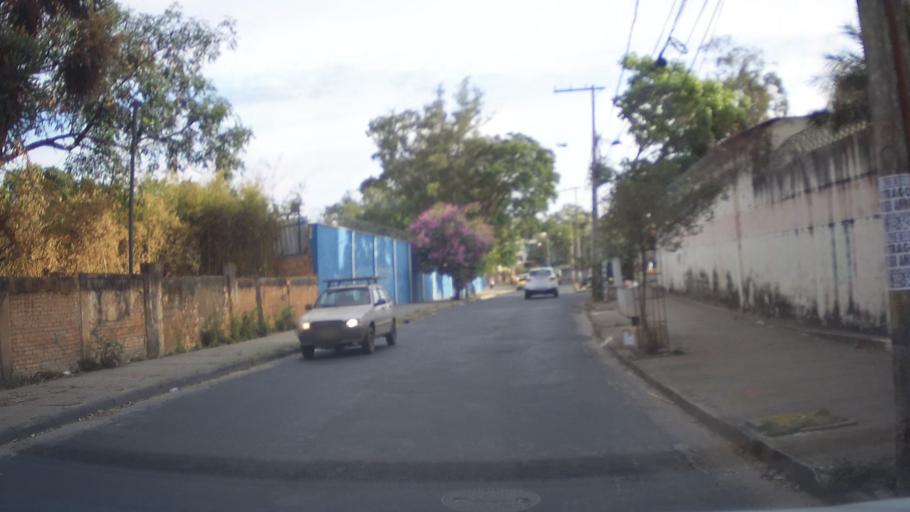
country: BR
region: Minas Gerais
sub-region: Belo Horizonte
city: Belo Horizonte
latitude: -19.8660
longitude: -43.9960
